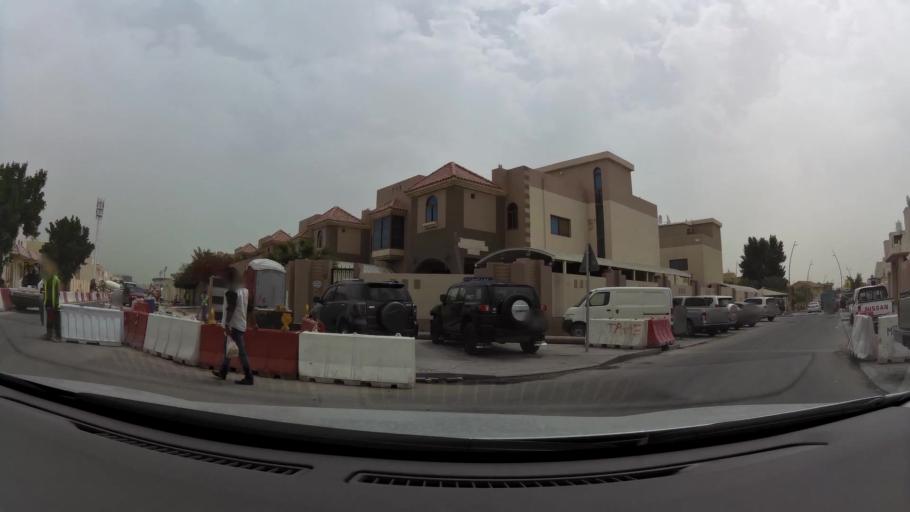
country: QA
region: Baladiyat ad Dawhah
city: Doha
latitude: 25.2591
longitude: 51.5122
